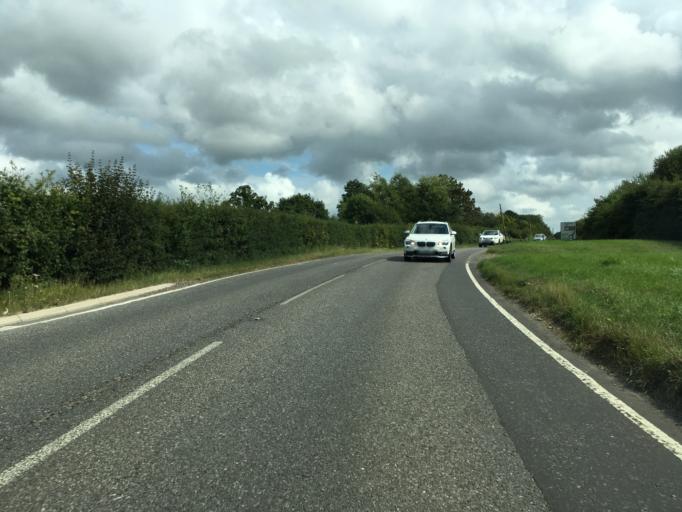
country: GB
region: England
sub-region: Kent
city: Tenterden
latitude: 51.0984
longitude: 0.6866
